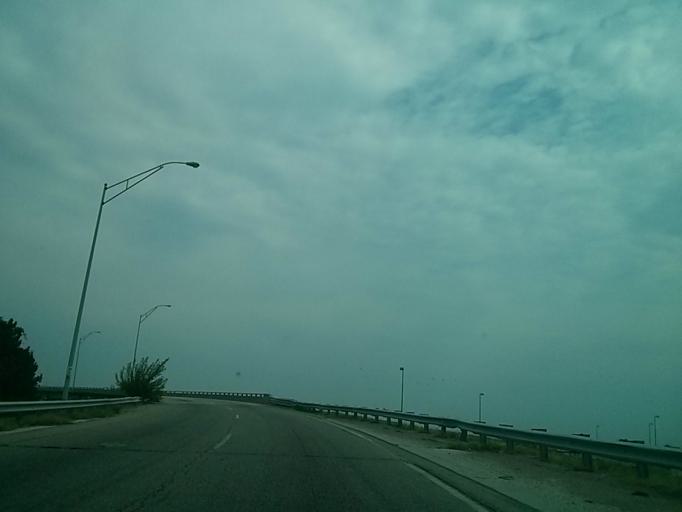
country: US
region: Oklahoma
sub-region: Tulsa County
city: Owasso
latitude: 36.1640
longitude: -95.8600
